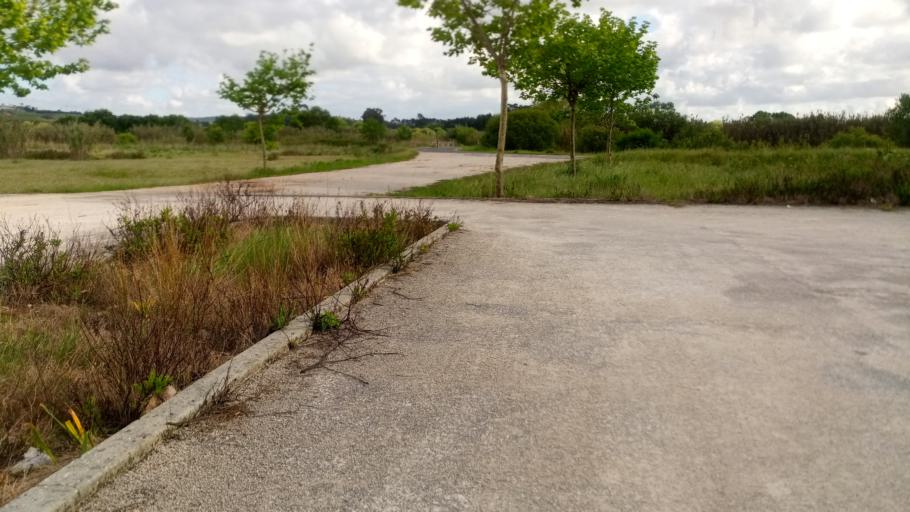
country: PT
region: Leiria
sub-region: Obidos
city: Obidos
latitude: 39.3902
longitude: -9.2007
